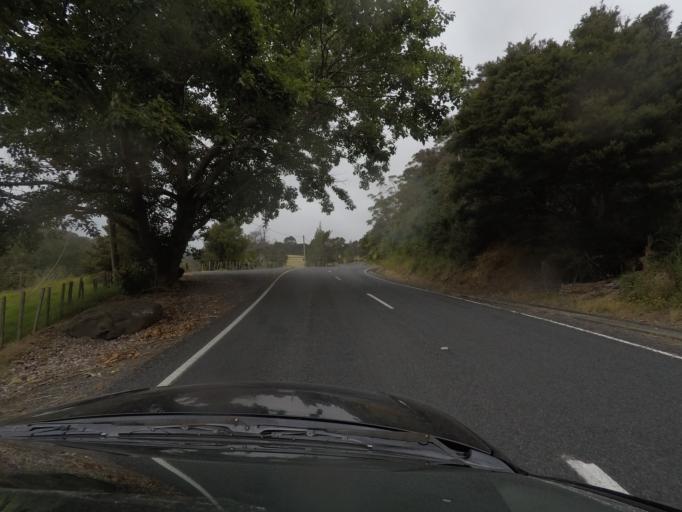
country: NZ
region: Auckland
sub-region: Auckland
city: Warkworth
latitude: -36.2787
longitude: 174.6968
